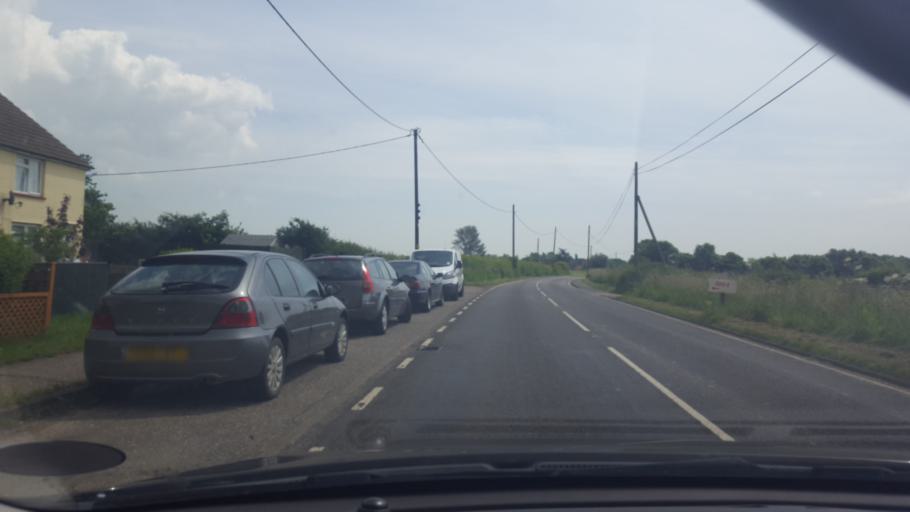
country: GB
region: England
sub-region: Essex
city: Great Bentley
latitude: 51.8830
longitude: 1.1124
